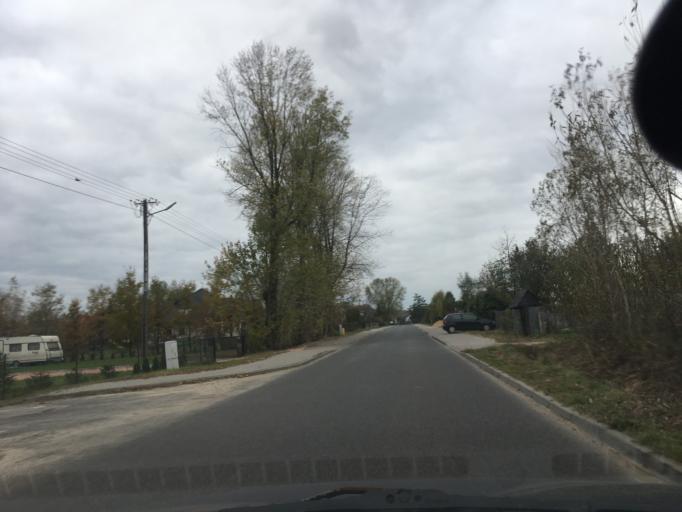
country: PL
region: Lodz Voivodeship
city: Zabia Wola
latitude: 52.0284
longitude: 20.6969
